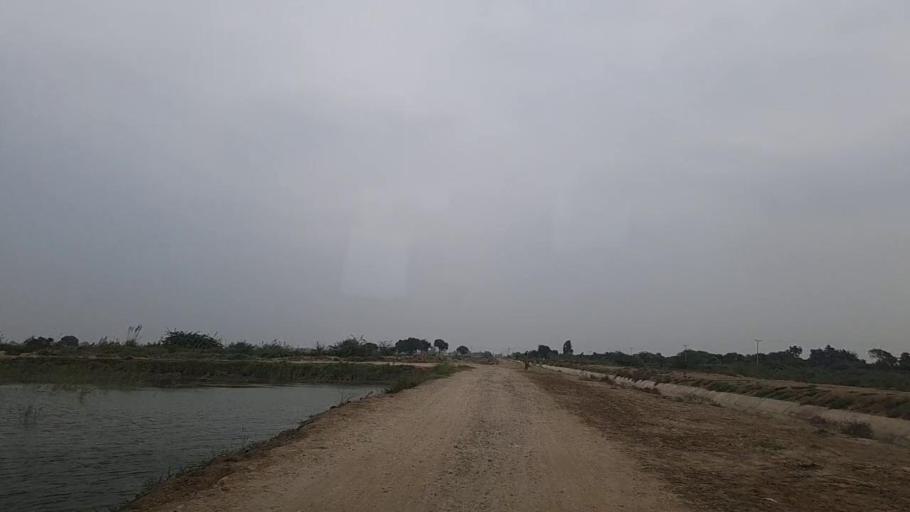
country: PK
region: Sindh
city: Mirpur Sakro
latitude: 24.6155
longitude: 67.7176
